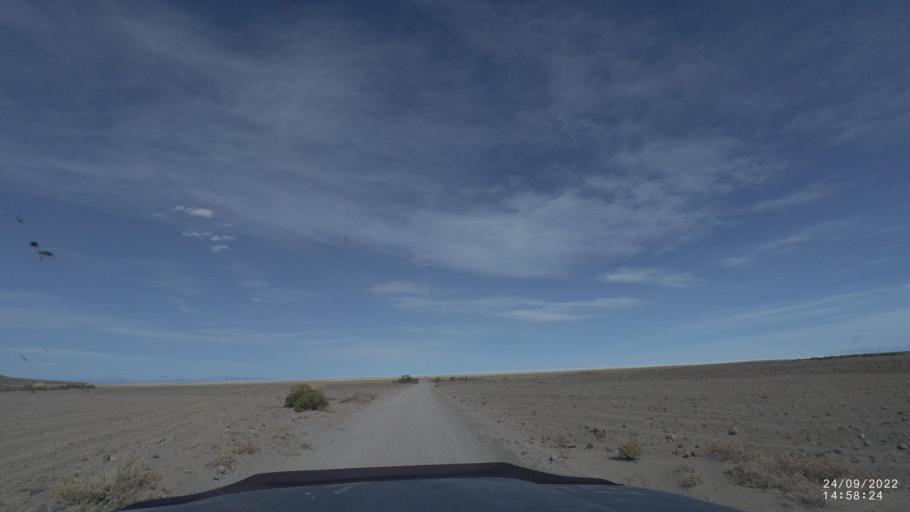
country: BO
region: Potosi
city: Colchani
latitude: -19.8610
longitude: -67.5679
